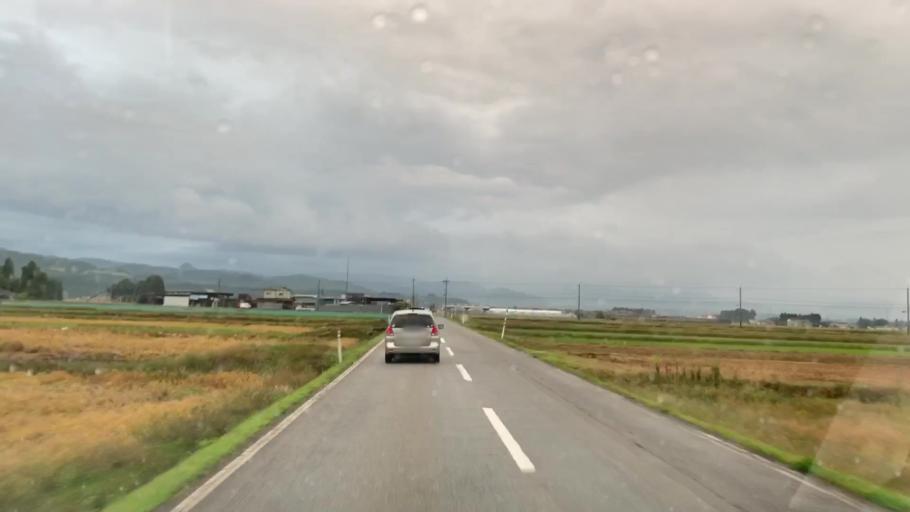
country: JP
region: Toyama
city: Kamiichi
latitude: 36.6430
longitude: 137.3285
